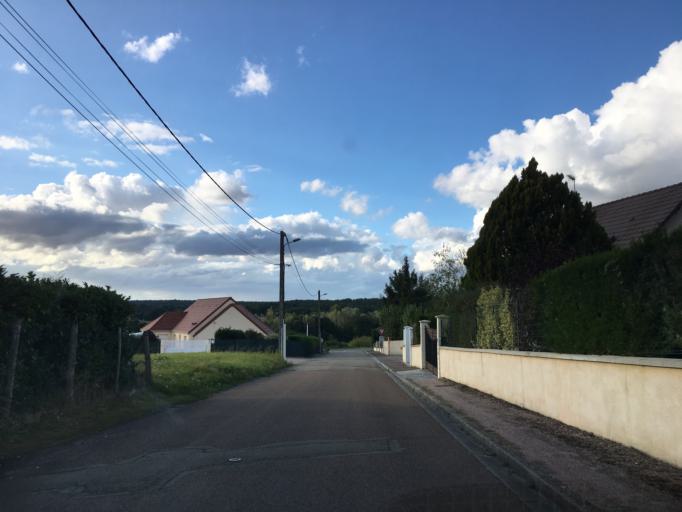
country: FR
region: Bourgogne
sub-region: Departement de l'Yonne
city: Saint-Georges-sur-Baulche
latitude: 47.8298
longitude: 3.5448
